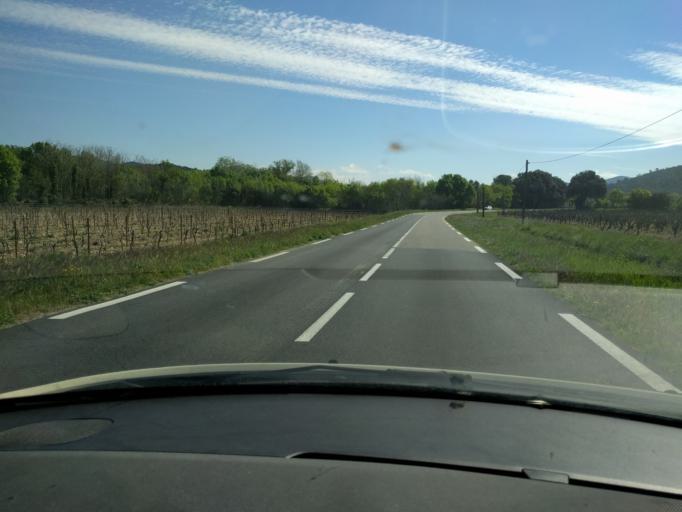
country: FR
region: Provence-Alpes-Cote d'Azur
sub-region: Departement du Var
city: Pierrefeu-du-Var
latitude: 43.2324
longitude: 6.1774
